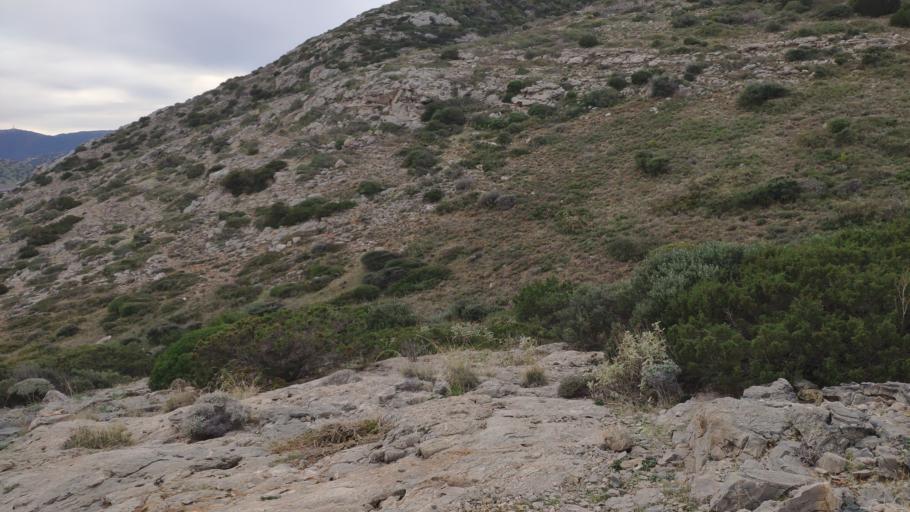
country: GR
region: Attica
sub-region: Nomarchia Anatolikis Attikis
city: Limin Mesoyaias
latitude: 37.9035
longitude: 24.0447
